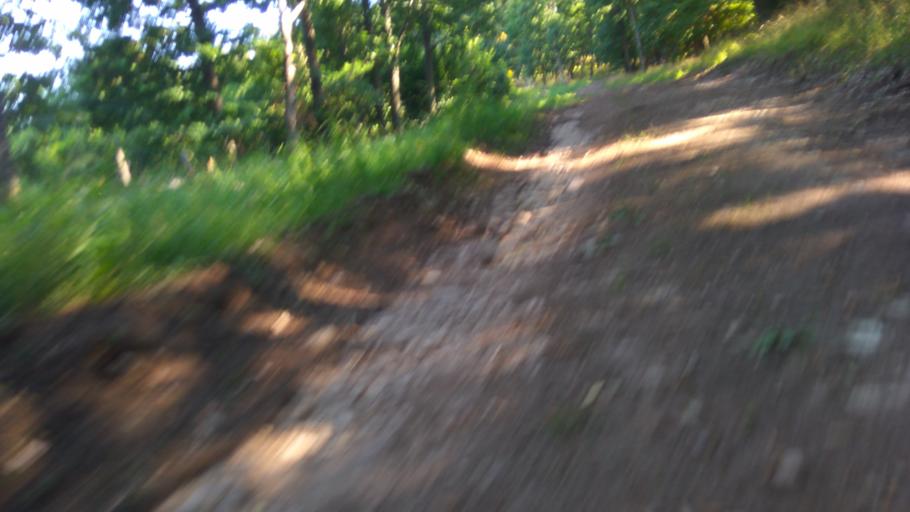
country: SK
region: Nitriansky
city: Sahy
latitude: 47.9823
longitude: 18.9563
